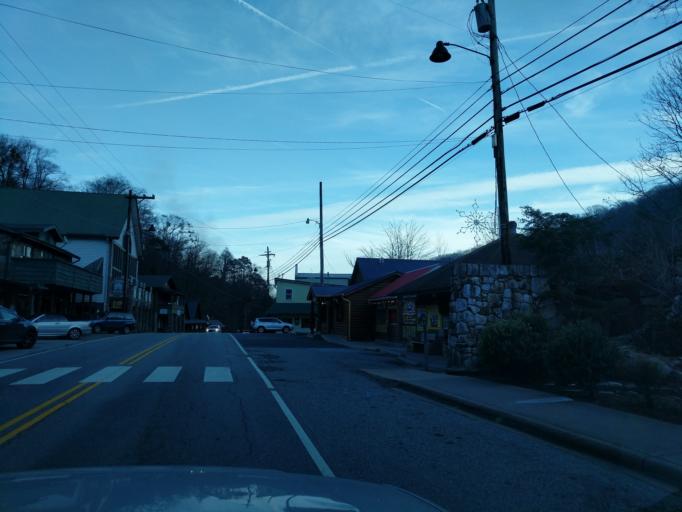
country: US
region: North Carolina
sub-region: Rutherford County
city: Lake Lure
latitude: 35.4398
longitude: -82.2484
